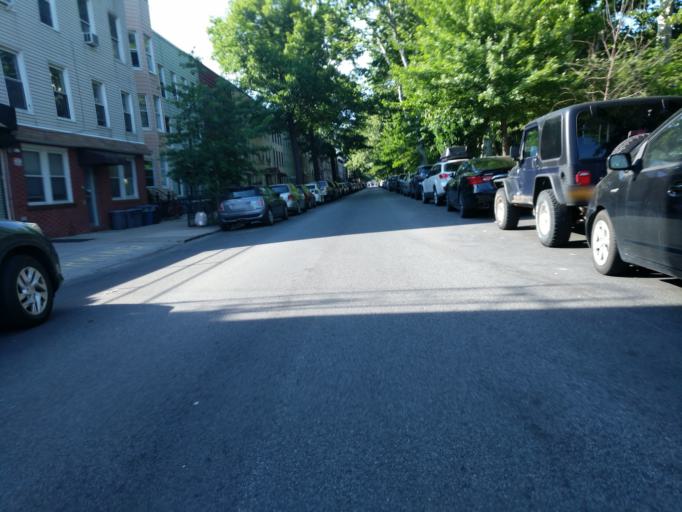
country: US
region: New York
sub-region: Queens County
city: Long Island City
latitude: 40.7232
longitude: -73.9441
